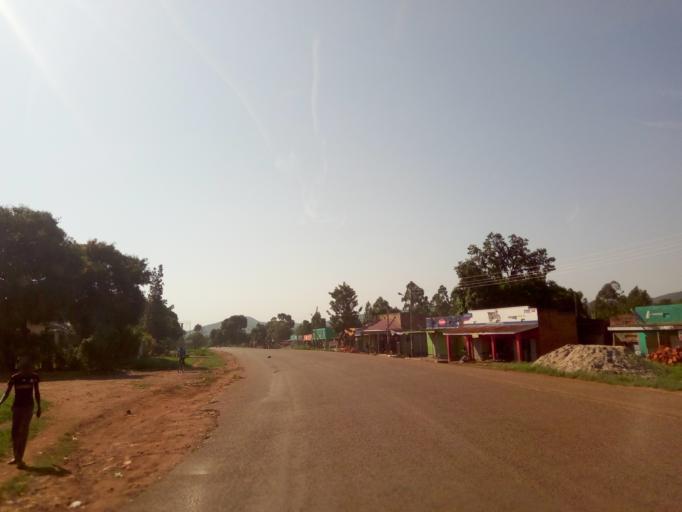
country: UG
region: Western Region
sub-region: Masindi District
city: Masindi
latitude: 1.6765
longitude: 31.7298
